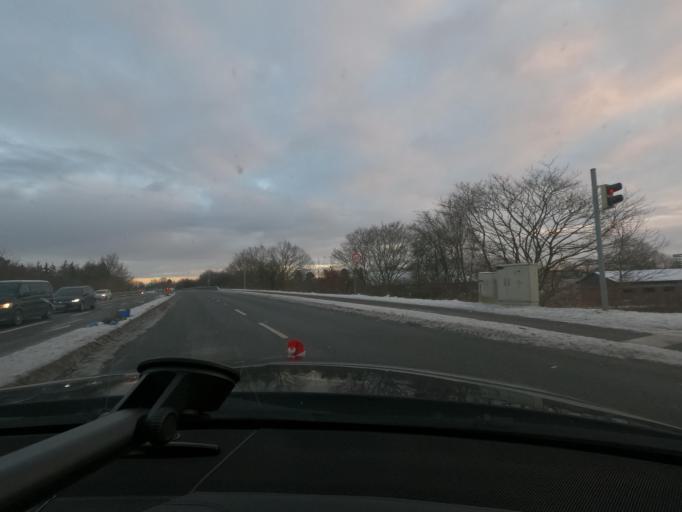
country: DE
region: Schleswig-Holstein
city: Flensburg
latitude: 54.7674
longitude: 9.4205
